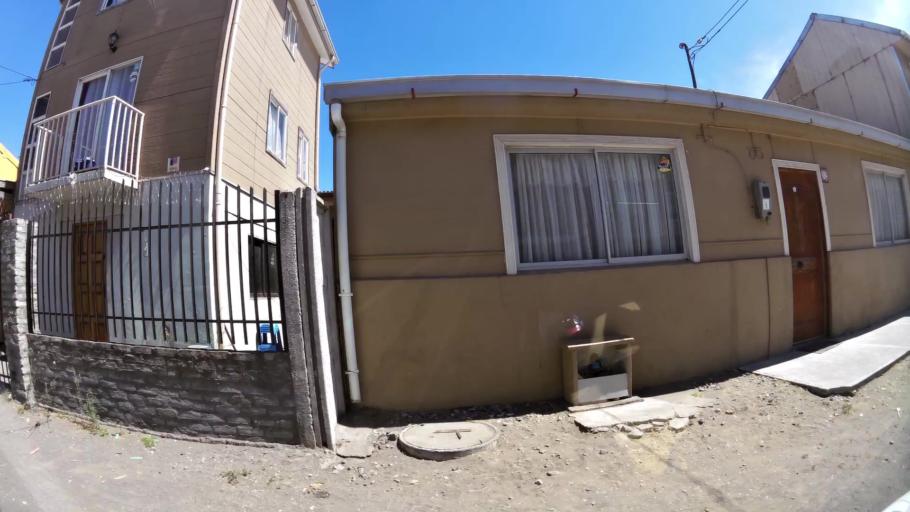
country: CL
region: Biobio
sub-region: Provincia de Concepcion
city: Talcahuano
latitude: -36.7262
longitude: -73.1053
